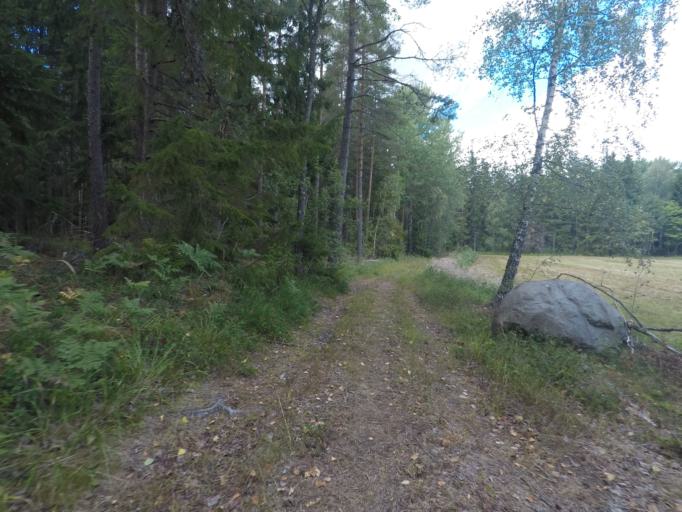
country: SE
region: Soedermanland
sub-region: Eskilstuna Kommun
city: Kvicksund
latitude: 59.4010
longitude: 16.3044
